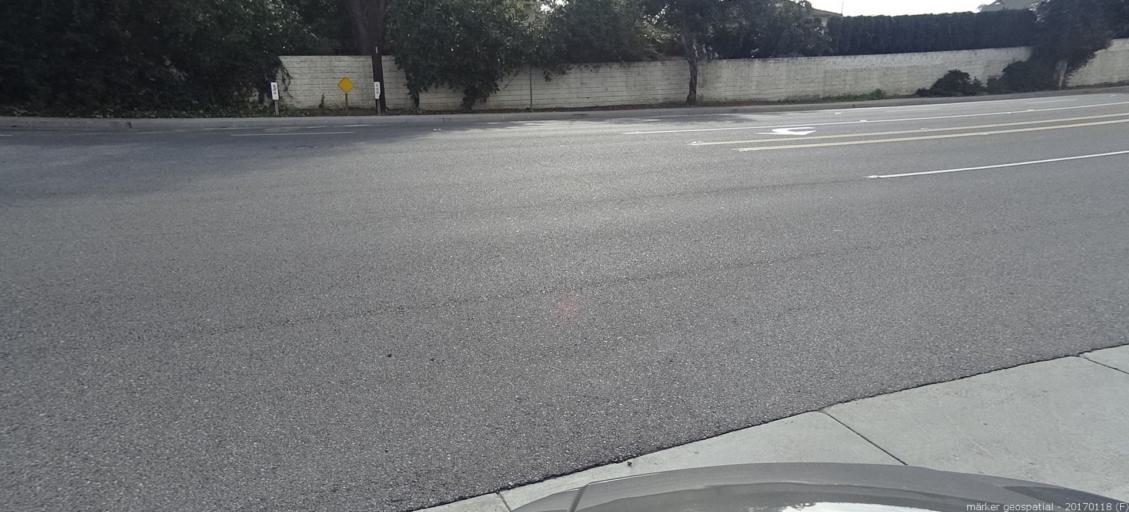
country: US
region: California
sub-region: Orange County
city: North Tustin
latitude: 33.7715
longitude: -117.7910
